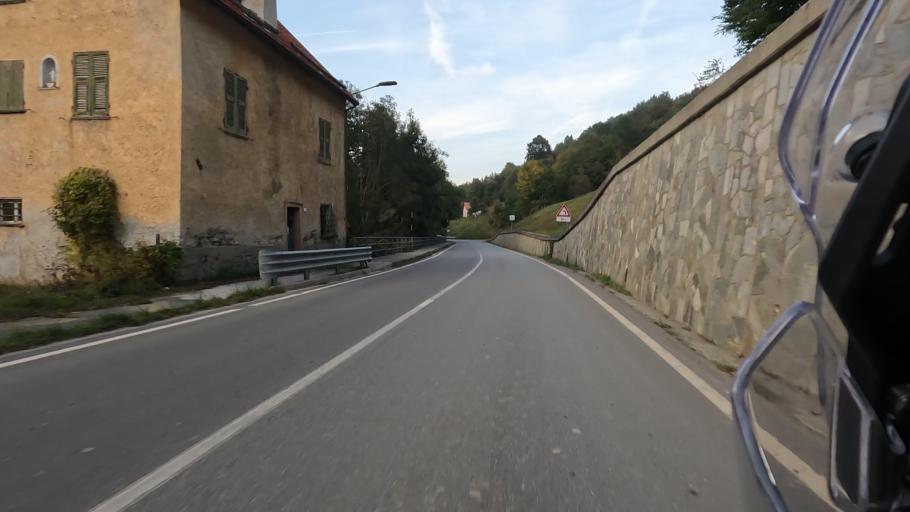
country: IT
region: Liguria
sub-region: Provincia di Savona
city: Sassello
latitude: 44.4670
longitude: 8.4841
